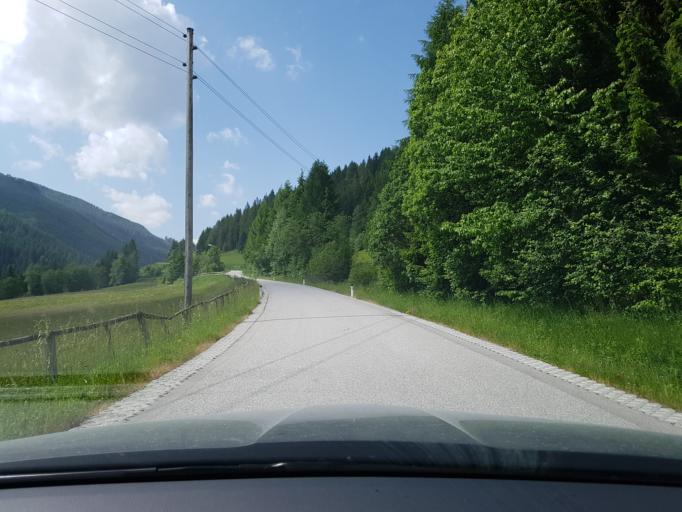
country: AT
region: Salzburg
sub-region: Politischer Bezirk Tamsweg
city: Thomatal
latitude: 47.0742
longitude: 13.7243
